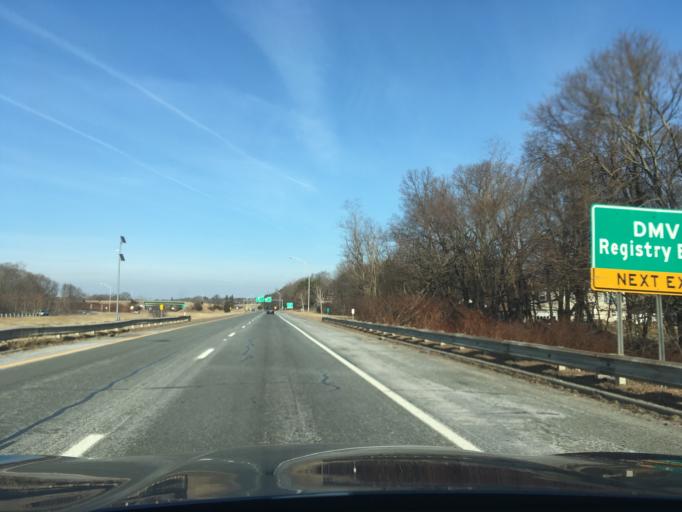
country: US
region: Rhode Island
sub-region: Providence County
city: Cranston
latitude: 41.7485
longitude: -71.4837
